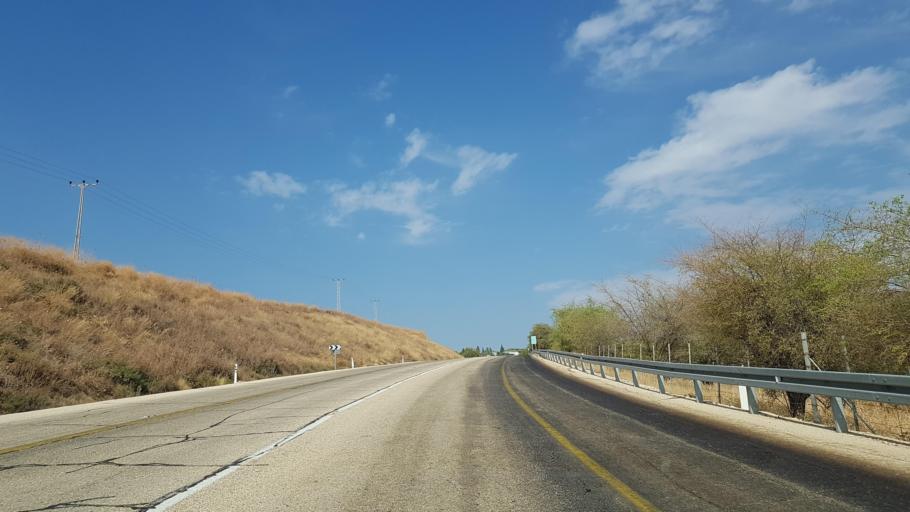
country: SY
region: Quneitra
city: Al Butayhah
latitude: 32.9001
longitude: 35.5967
